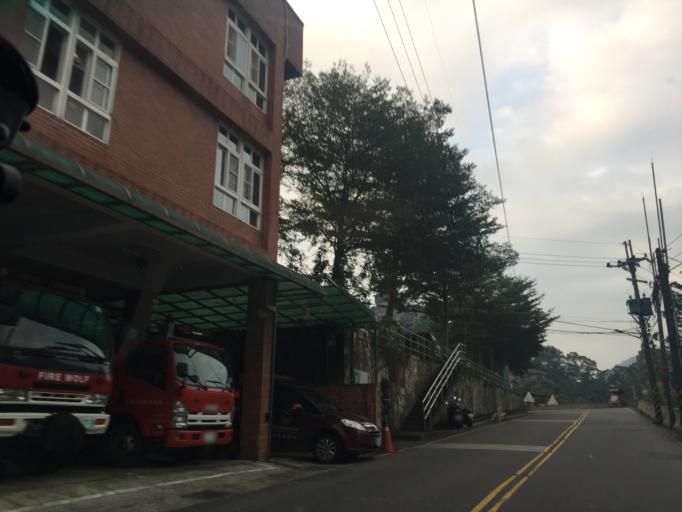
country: TW
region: Taipei
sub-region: Taipei
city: Banqiao
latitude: 24.8639
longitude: 121.5487
